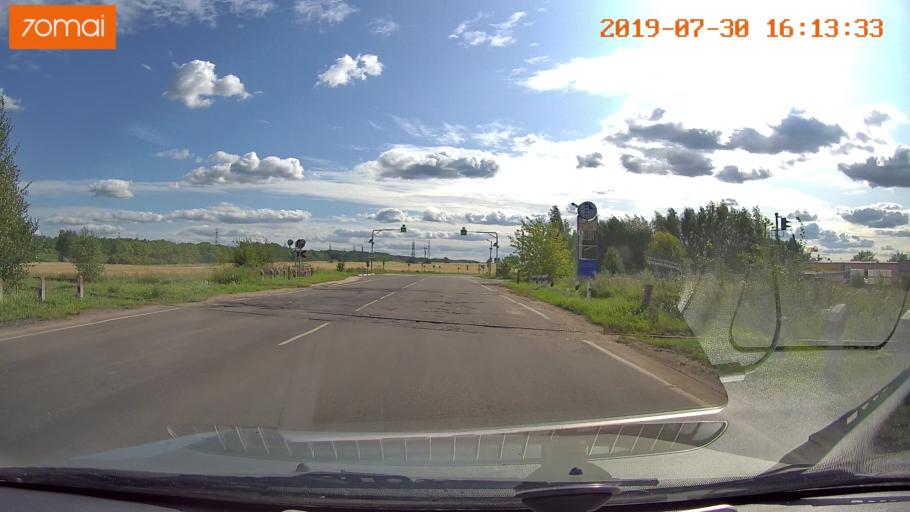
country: RU
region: Moskovskaya
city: Voskresensk
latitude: 55.2894
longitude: 38.6902
